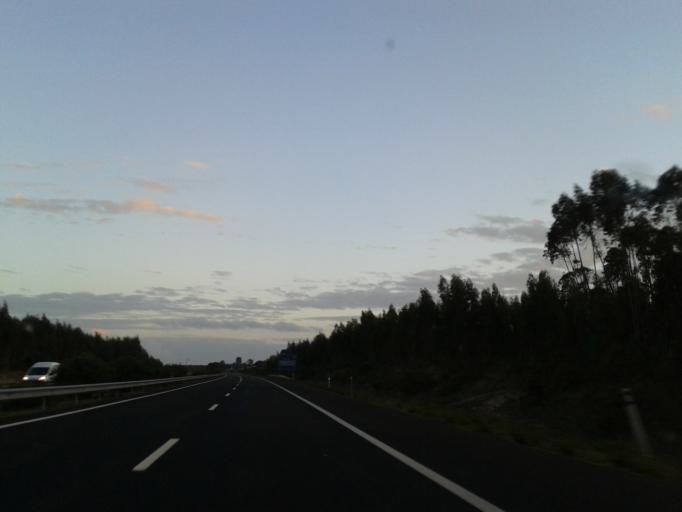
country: PT
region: Santarem
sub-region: Benavente
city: Poceirao
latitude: 38.7322
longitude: -8.6757
